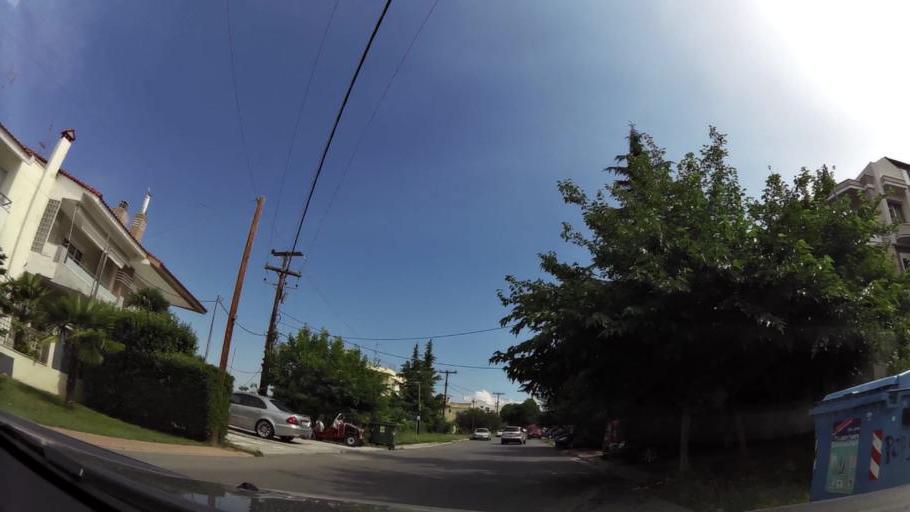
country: GR
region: Central Macedonia
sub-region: Nomos Thessalonikis
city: Panorama
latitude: 40.5785
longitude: 23.0063
